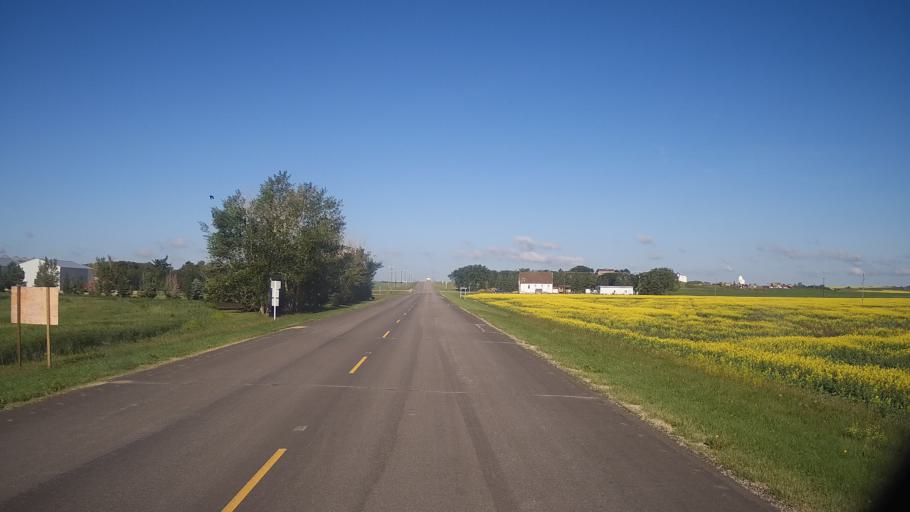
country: CA
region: Saskatchewan
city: Watrous
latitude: 51.6781
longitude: -105.3995
